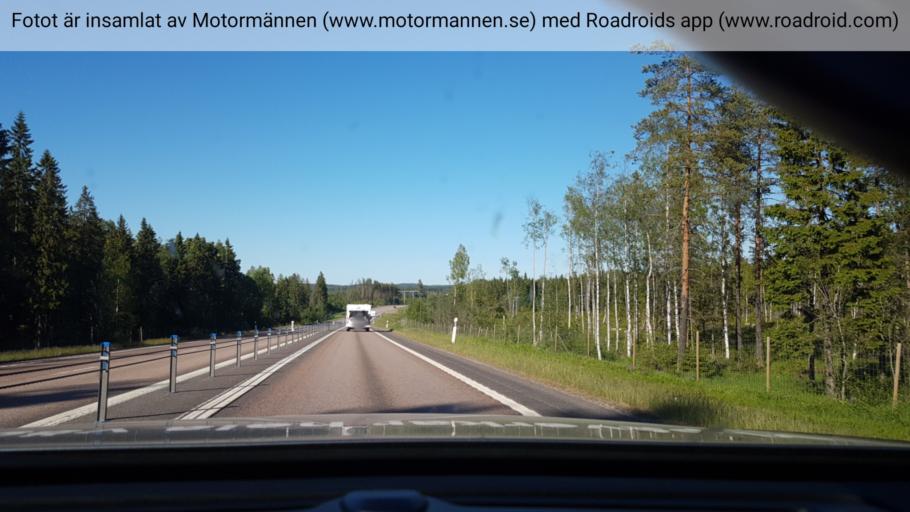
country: SE
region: Vaesternorrland
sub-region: Haernoesands Kommun
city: Haernoesand
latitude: 62.5726
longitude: 17.7455
